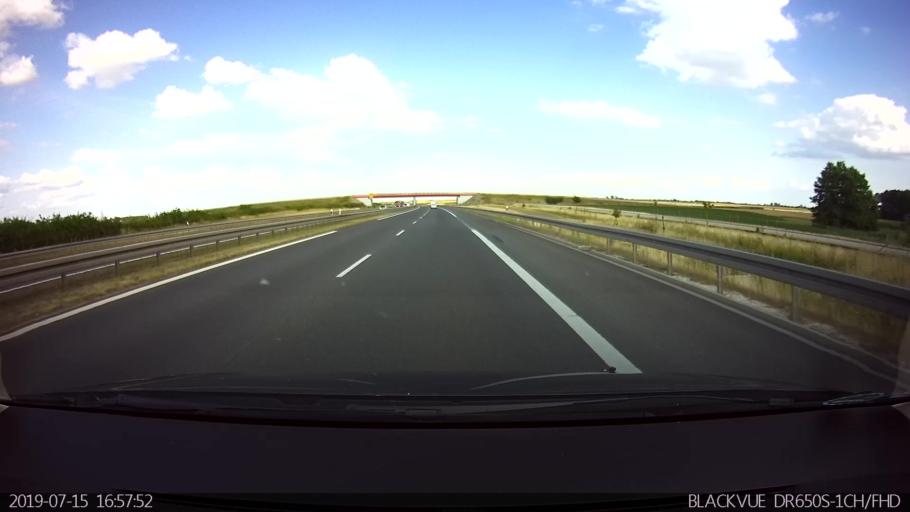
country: PL
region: Lower Silesian Voivodeship
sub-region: Powiat olesnicki
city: Dobroszyce
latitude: 51.2217
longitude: 17.3156
